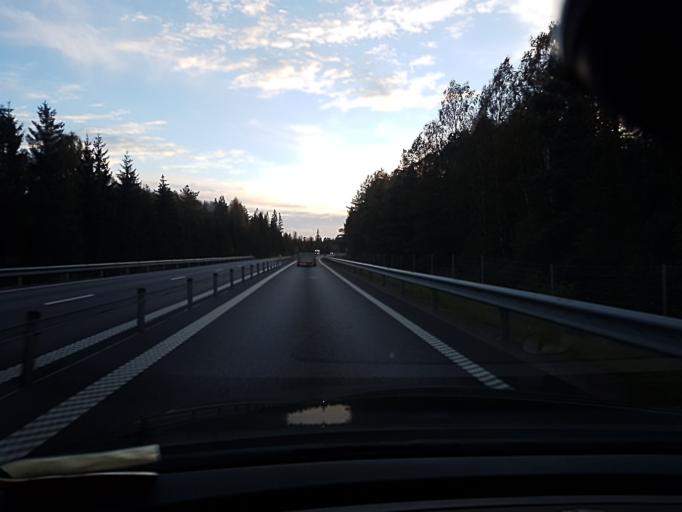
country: SE
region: Kronoberg
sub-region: Ljungby Kommun
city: Ljungby
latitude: 56.7660
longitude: 13.7959
